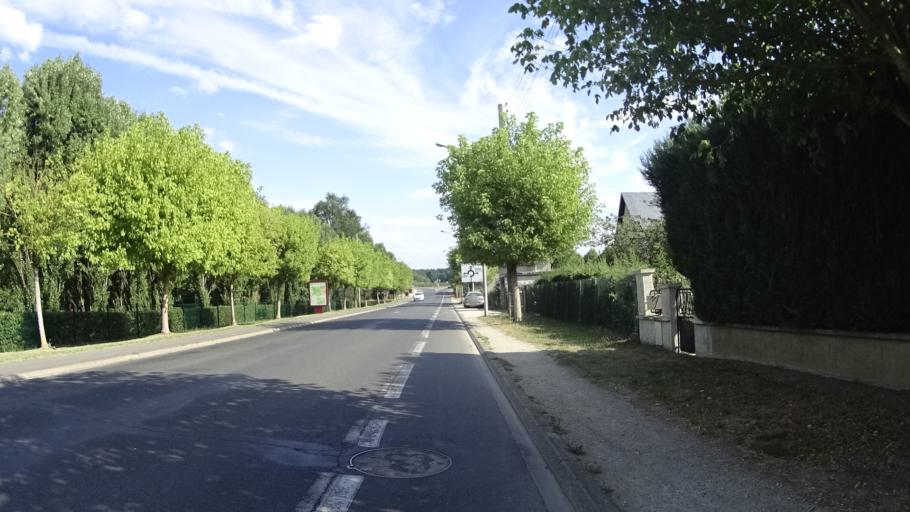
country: FR
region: Centre
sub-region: Departement du Loir-et-Cher
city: Chaumont-sur-Loire
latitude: 47.4887
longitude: 1.1879
